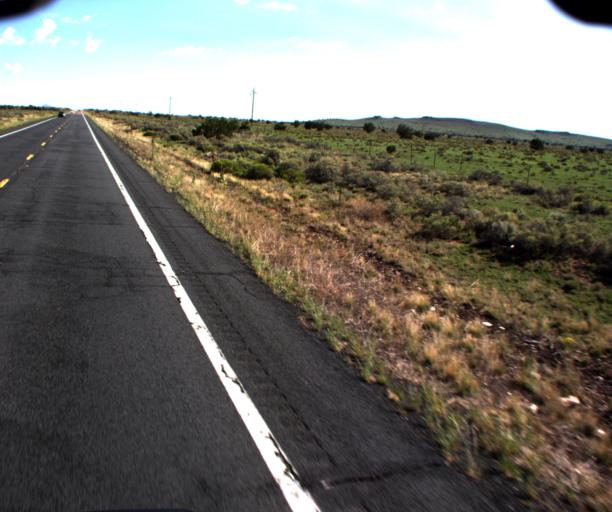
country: US
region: Arizona
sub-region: Coconino County
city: Williams
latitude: 35.5289
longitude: -112.1667
